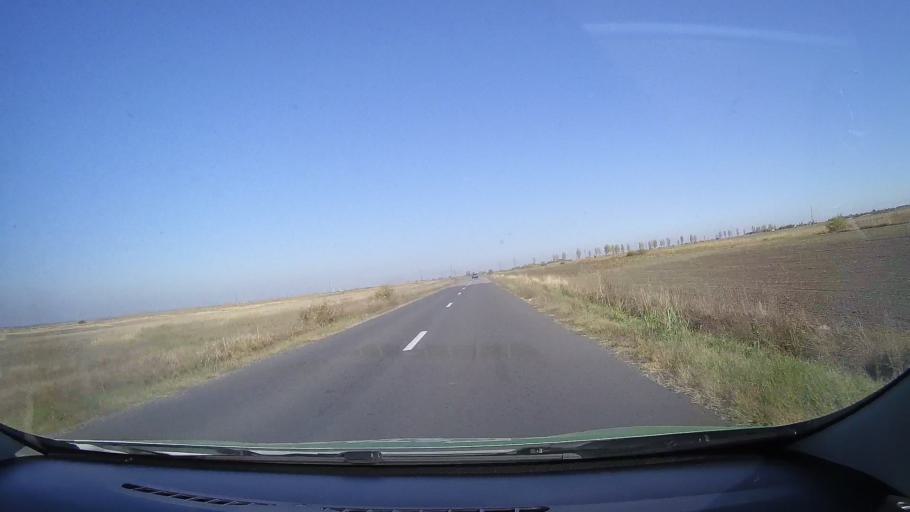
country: RO
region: Satu Mare
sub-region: Comuna Cauas
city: Cauas
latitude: 47.5909
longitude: 22.5469
